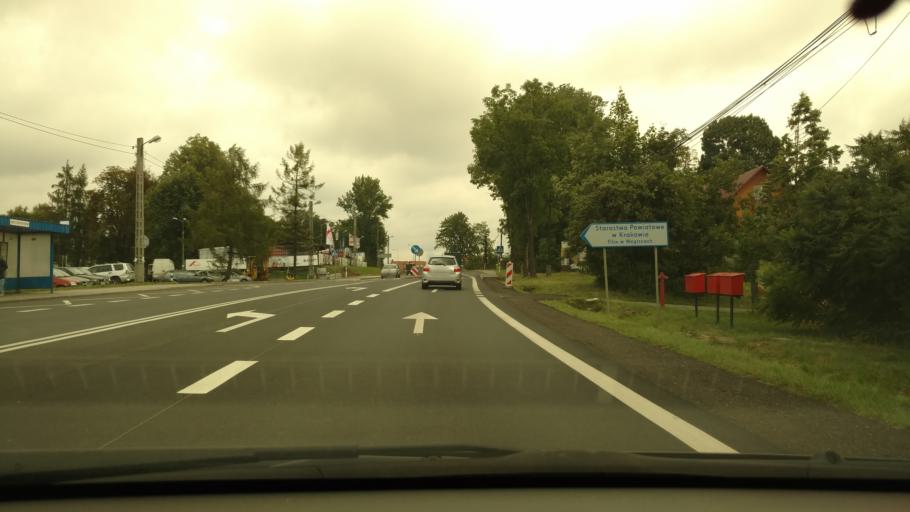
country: PL
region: Lesser Poland Voivodeship
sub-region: Powiat krakowski
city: Zielonki
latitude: 50.1138
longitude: 19.9665
